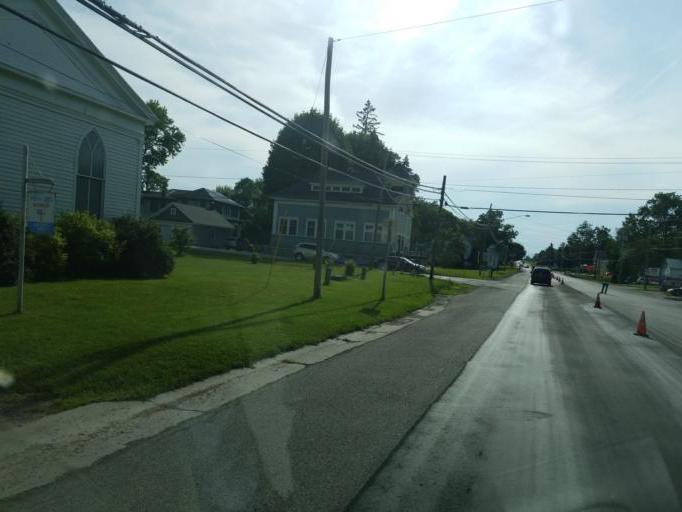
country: US
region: New York
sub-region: Genesee County
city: Le Roy
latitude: 42.9816
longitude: -78.0729
